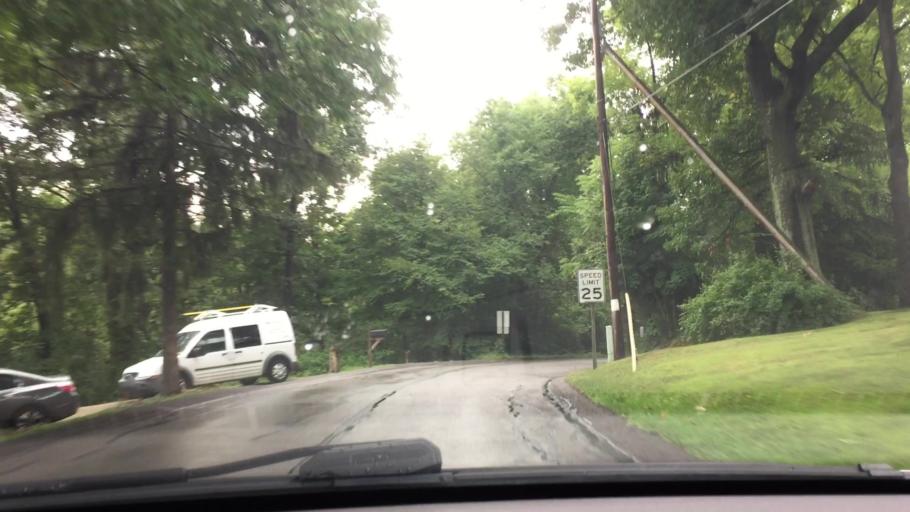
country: US
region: Pennsylvania
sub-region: Washington County
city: Cecil-Bishop
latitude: 40.3077
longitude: -80.2013
